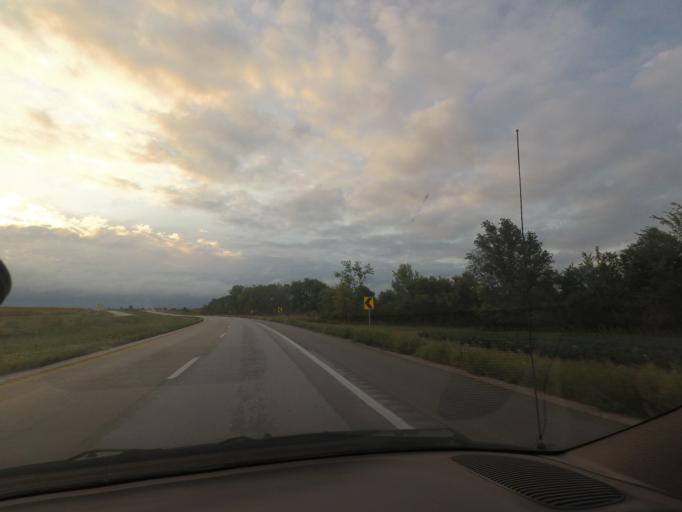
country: US
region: Missouri
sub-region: Shelby County
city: Shelbina
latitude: 39.6897
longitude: -92.0206
